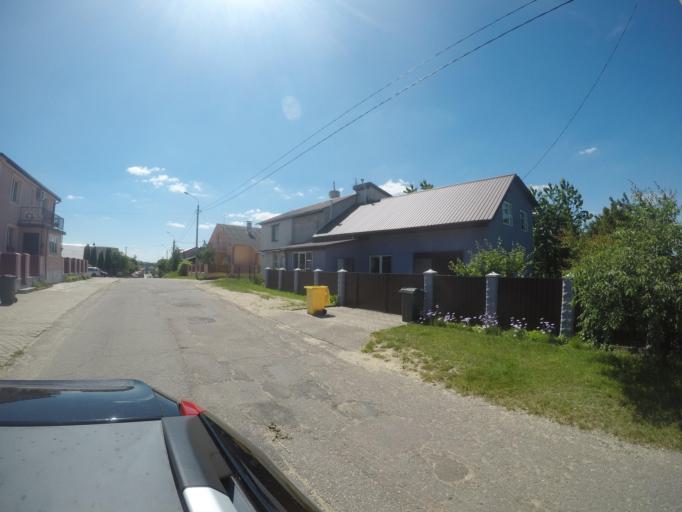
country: BY
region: Grodnenskaya
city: Hrodna
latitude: 53.6927
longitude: 23.8180
